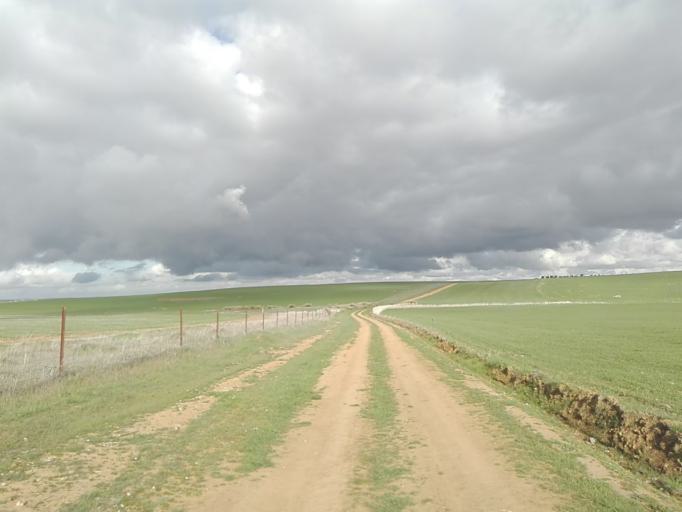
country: ES
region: Extremadura
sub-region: Provincia de Badajoz
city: Llerena
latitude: 38.2832
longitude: -6.0184
